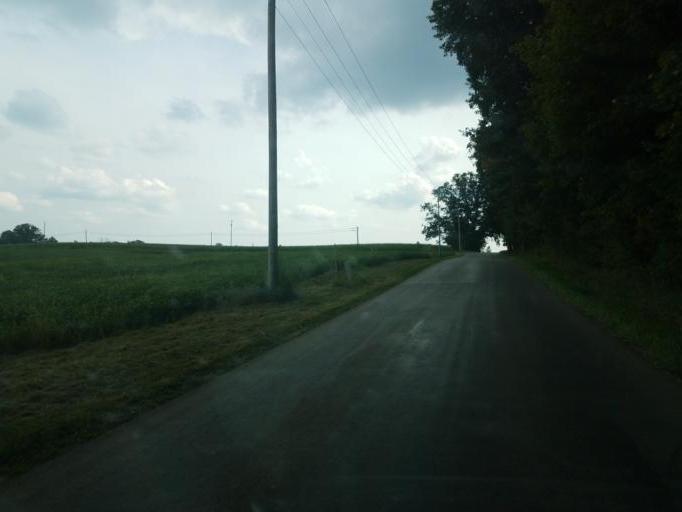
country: US
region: Ohio
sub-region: Knox County
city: Gambier
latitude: 40.3596
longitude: -82.3544
